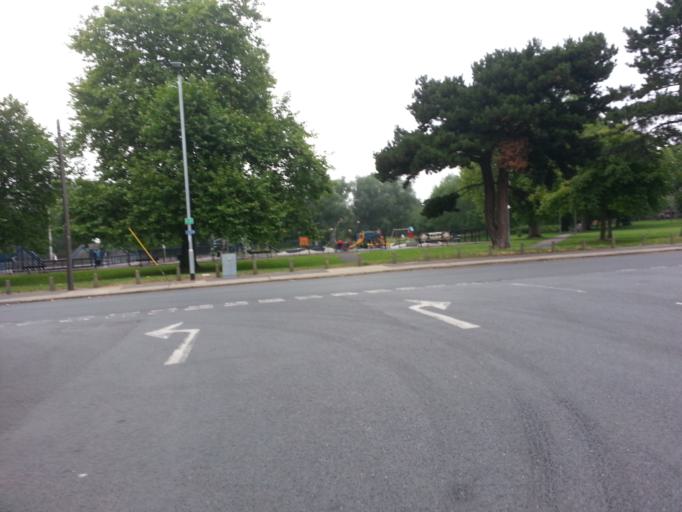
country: GB
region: England
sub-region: Suffolk
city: Ipswich
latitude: 52.0553
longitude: 1.1429
